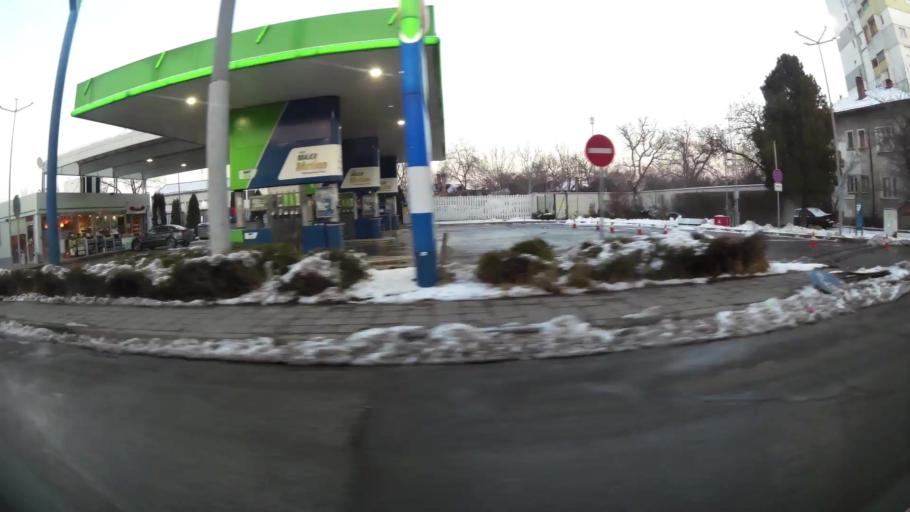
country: BG
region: Sofia-Capital
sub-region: Stolichna Obshtina
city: Sofia
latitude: 42.6909
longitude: 23.3698
